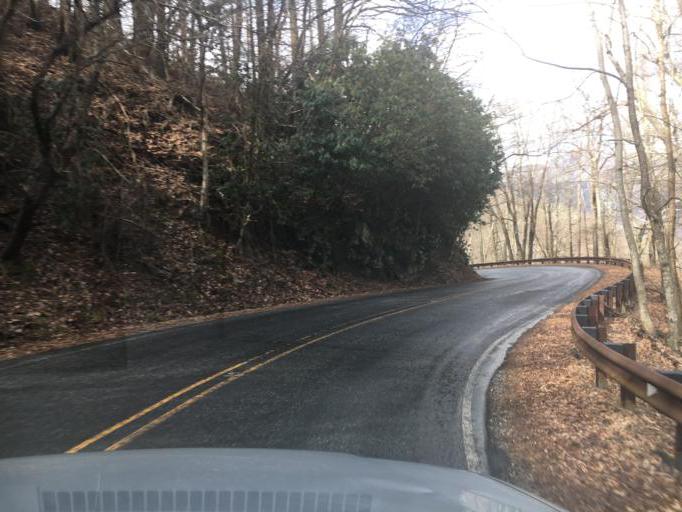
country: US
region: North Carolina
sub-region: Transylvania County
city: Brevard
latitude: 35.3671
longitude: -82.8007
